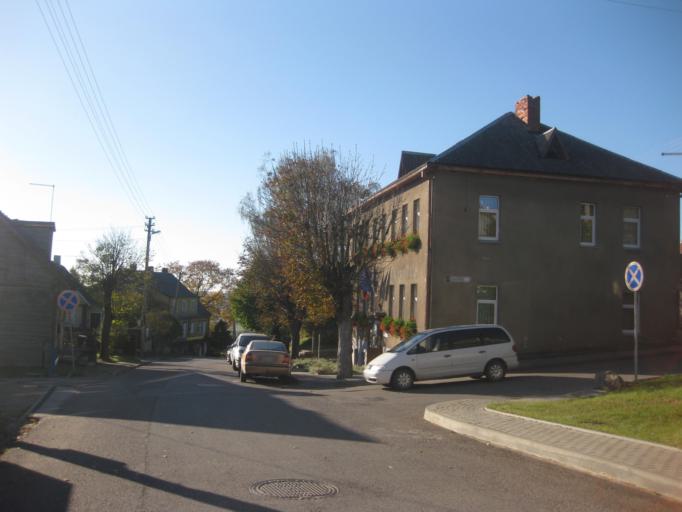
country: LT
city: Vilkija
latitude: 55.0389
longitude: 23.5874
